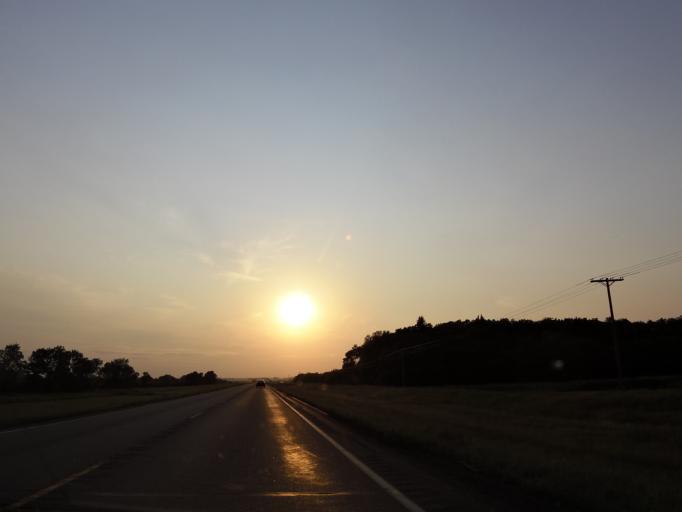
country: US
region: North Dakota
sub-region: Grand Forks County
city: Larimore
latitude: 47.7441
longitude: -97.6101
